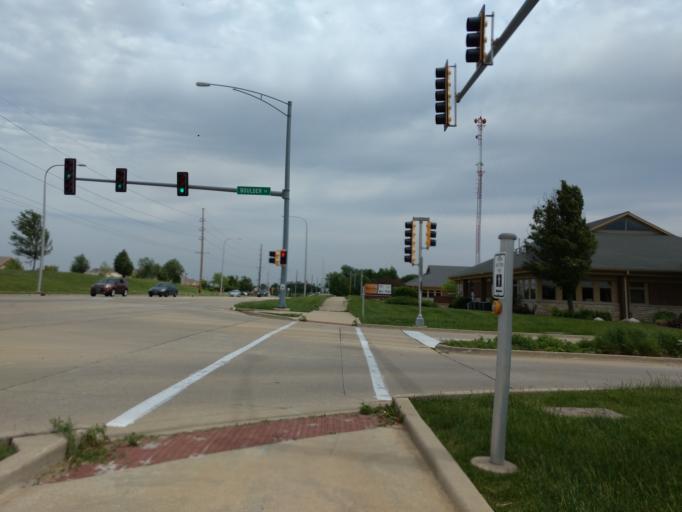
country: US
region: Illinois
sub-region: Champaign County
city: Urbana
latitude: 40.0837
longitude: -88.1883
